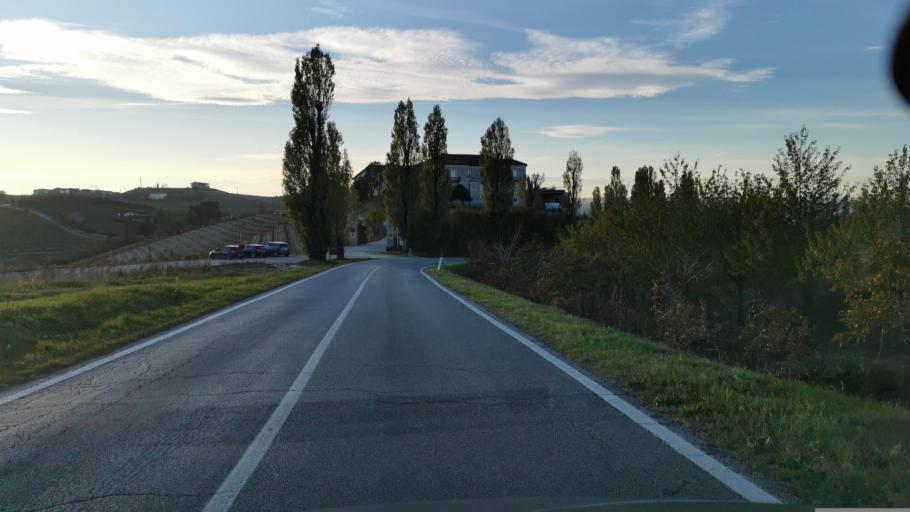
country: IT
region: Piedmont
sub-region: Provincia di Cuneo
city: Dogliani
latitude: 44.5215
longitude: 7.9494
